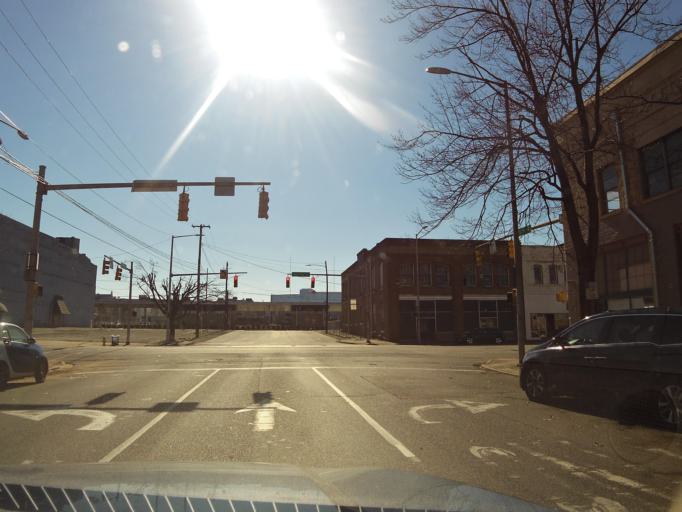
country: US
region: Alabama
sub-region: Jefferson County
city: Birmingham
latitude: 33.5127
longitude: -86.8101
